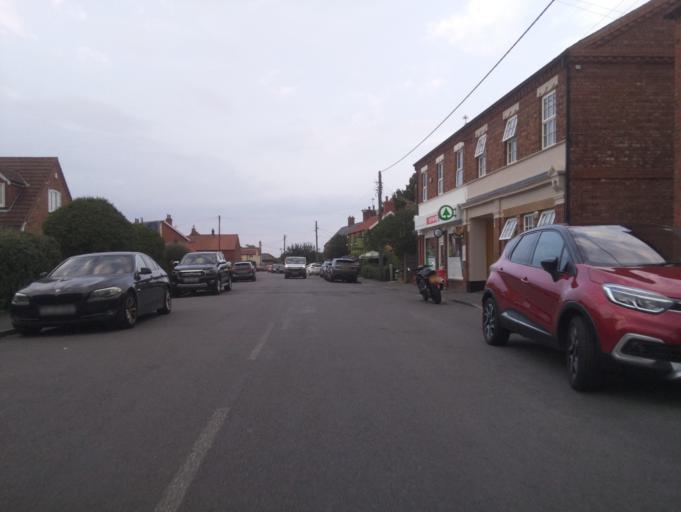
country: GB
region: England
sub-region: Lincolnshire
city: Skellingthorpe
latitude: 53.1299
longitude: -0.6387
